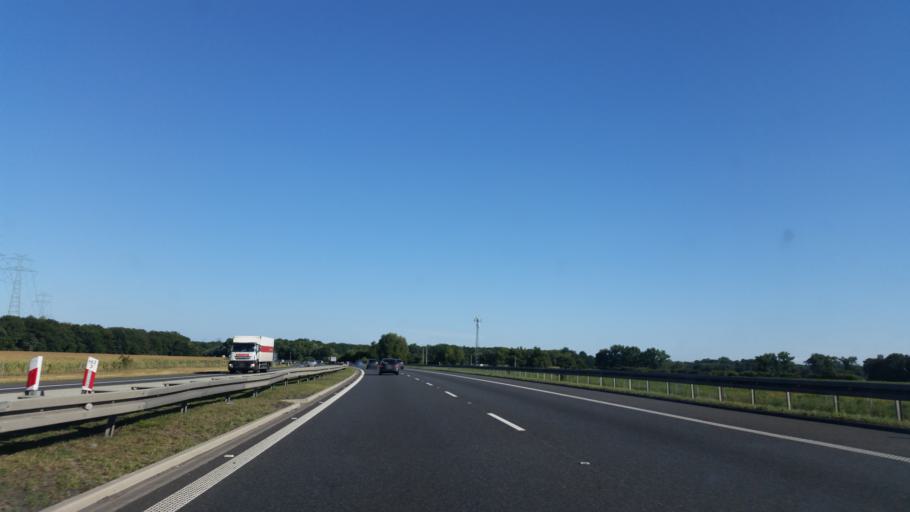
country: PL
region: Lower Silesian Voivodeship
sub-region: Powiat strzelinski
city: Wiazow
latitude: 50.8536
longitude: 17.2315
